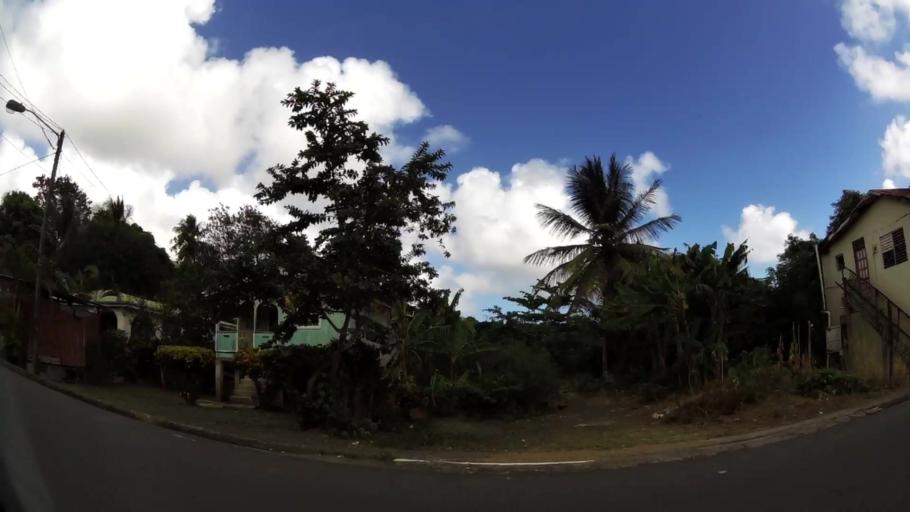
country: LC
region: Dennery Quarter
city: Dennery
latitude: 13.9331
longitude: -60.9329
